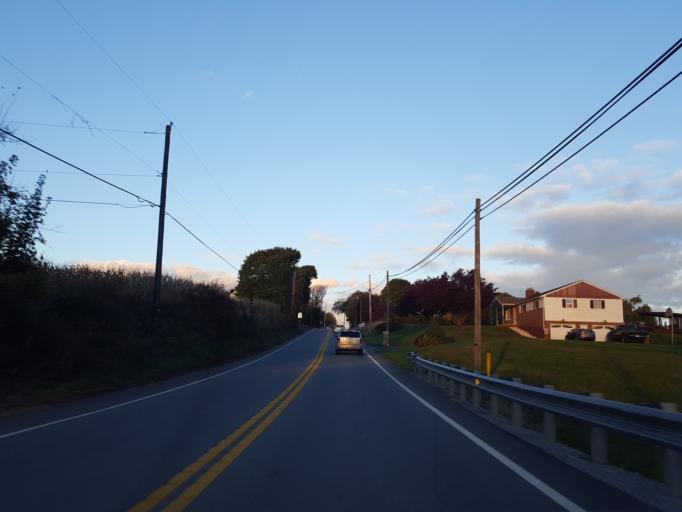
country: US
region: Pennsylvania
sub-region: York County
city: Windsor
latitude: 39.9392
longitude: -76.5280
